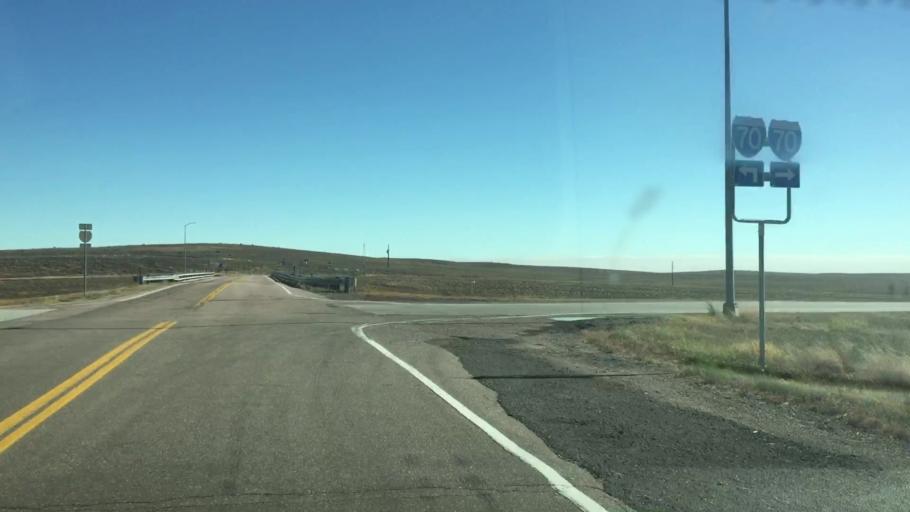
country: US
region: Colorado
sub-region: Lincoln County
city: Limon
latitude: 39.3118
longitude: -103.8263
